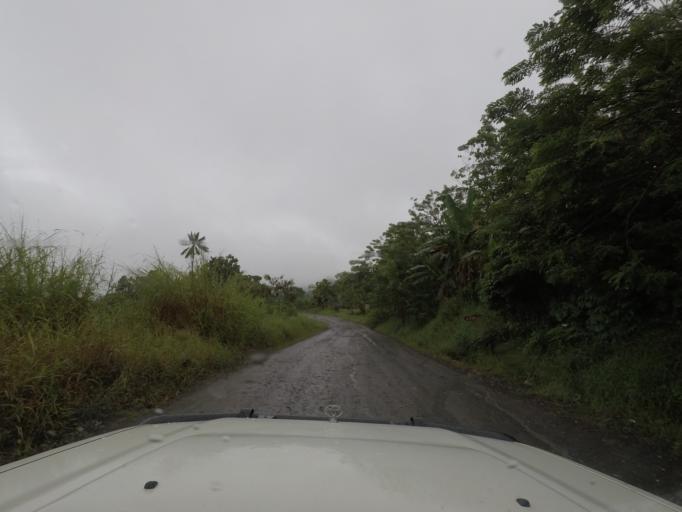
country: PG
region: Madang
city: Madang
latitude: -5.4711
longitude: 145.4835
